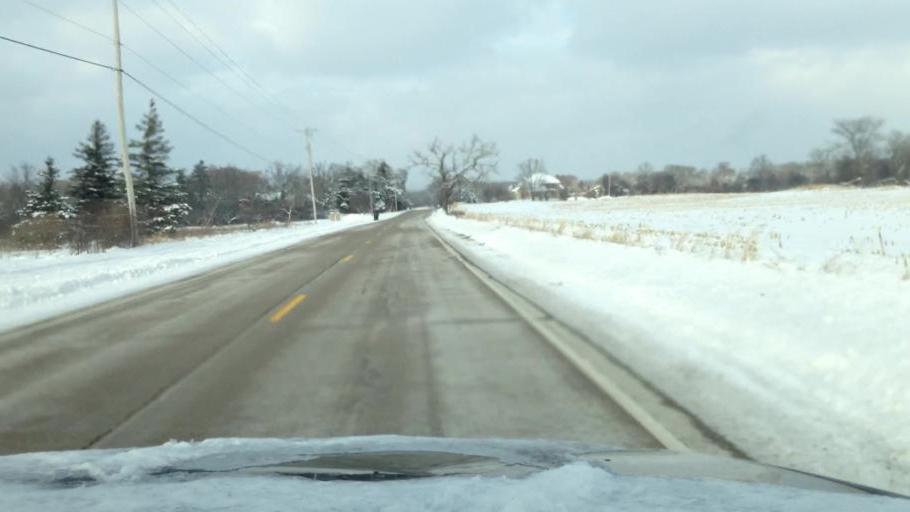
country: US
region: Wisconsin
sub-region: Waukesha County
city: North Prairie
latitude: 42.8837
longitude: -88.4202
